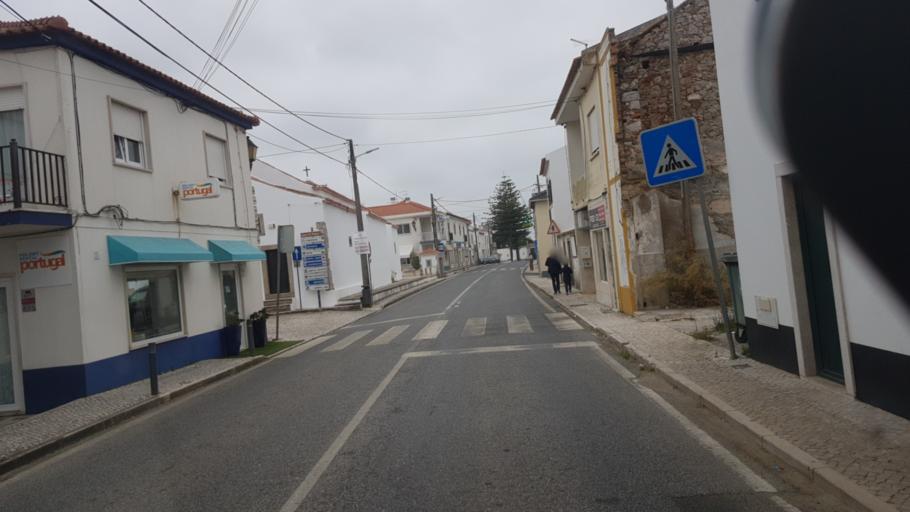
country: PT
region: Leiria
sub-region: Peniche
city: Atouguia da Baleia
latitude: 39.3314
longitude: -9.2703
